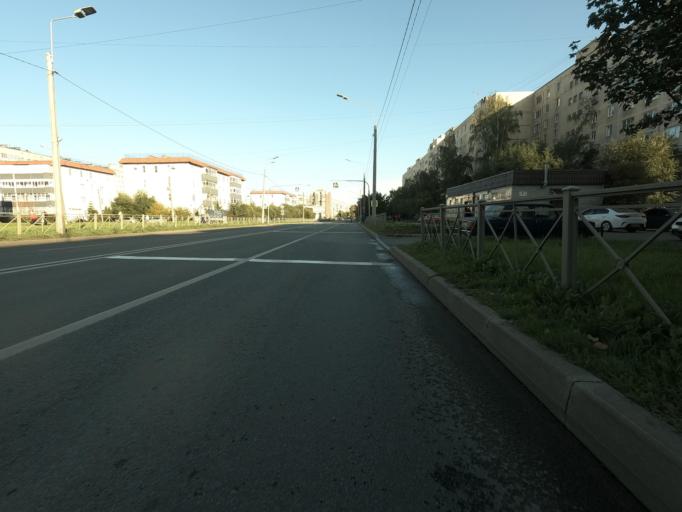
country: RU
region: St.-Petersburg
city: Kolpino
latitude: 59.7417
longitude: 30.5742
